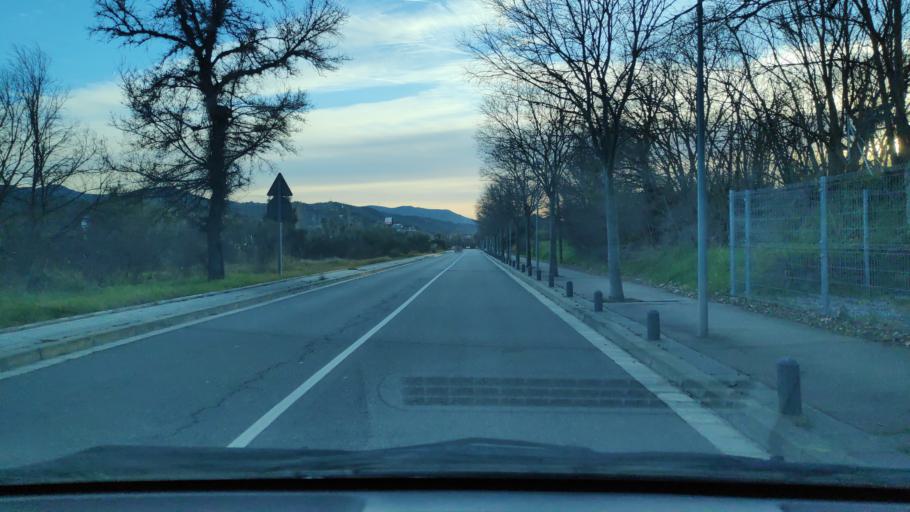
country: ES
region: Catalonia
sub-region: Provincia de Barcelona
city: Montmelo
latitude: 41.5634
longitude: 2.2581
